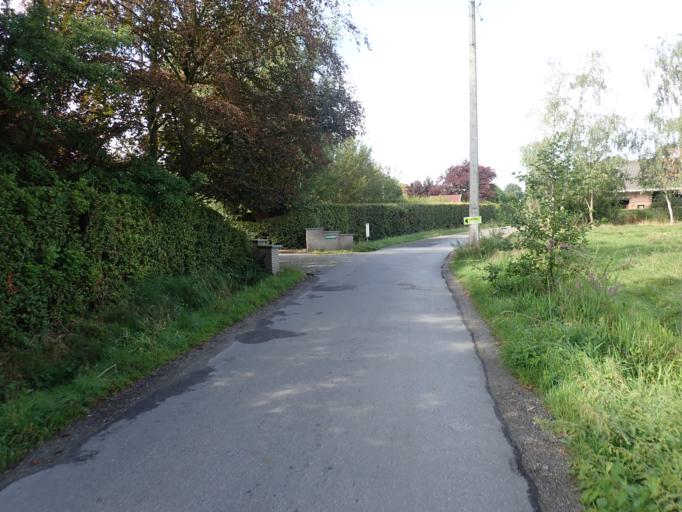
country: BE
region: Flanders
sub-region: Provincie Oost-Vlaanderen
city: Temse
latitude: 51.1246
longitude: 4.1857
